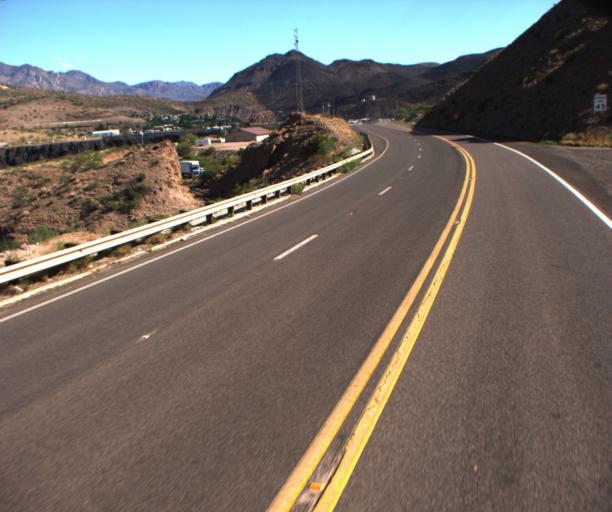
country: US
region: Arizona
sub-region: Greenlee County
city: Clifton
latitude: 33.0340
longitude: -109.2976
